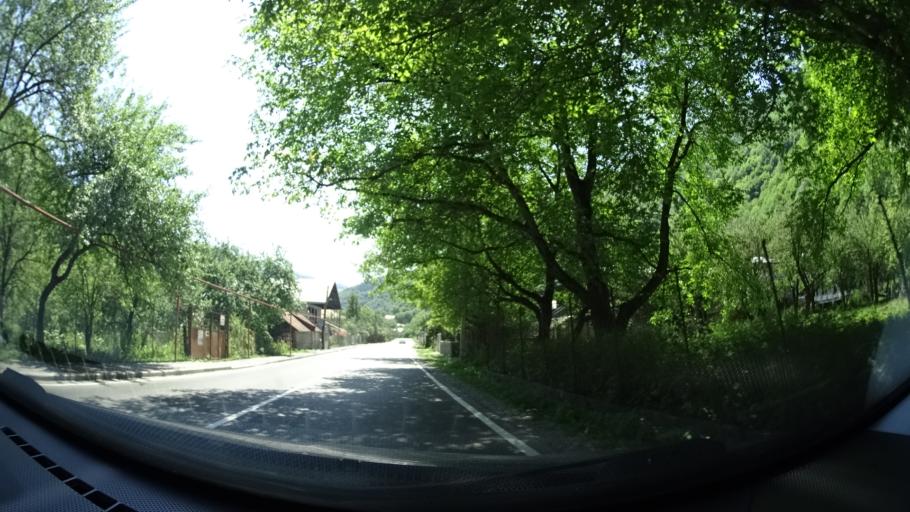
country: GE
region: Mtskheta-Mtianeti
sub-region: Dusheti
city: P'asanauri
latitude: 42.3594
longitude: 44.6853
